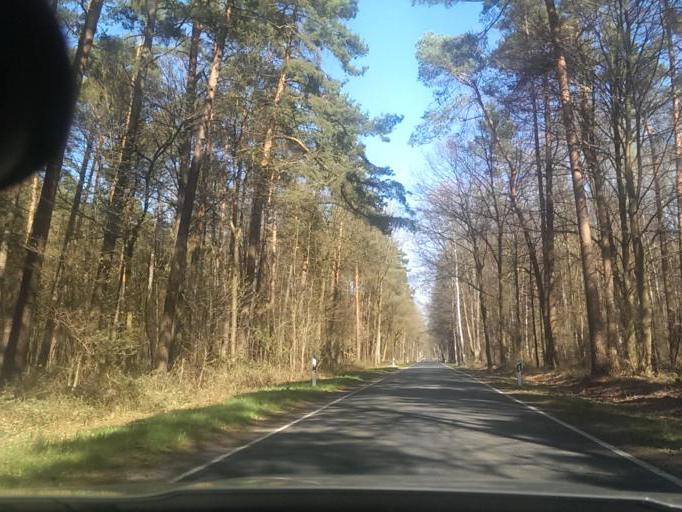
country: DE
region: Lower Saxony
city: Elze
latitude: 52.5307
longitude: 9.7000
